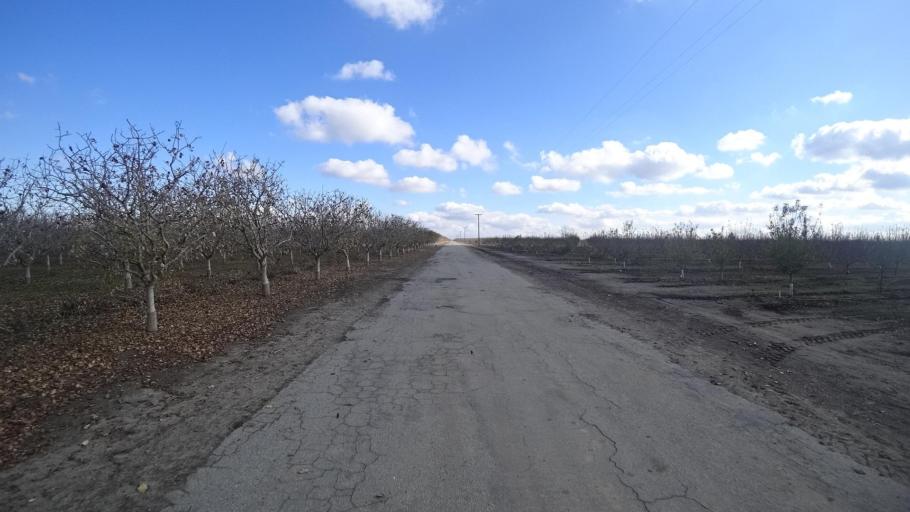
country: US
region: California
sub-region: Kern County
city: Wasco
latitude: 35.6669
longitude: -119.3200
